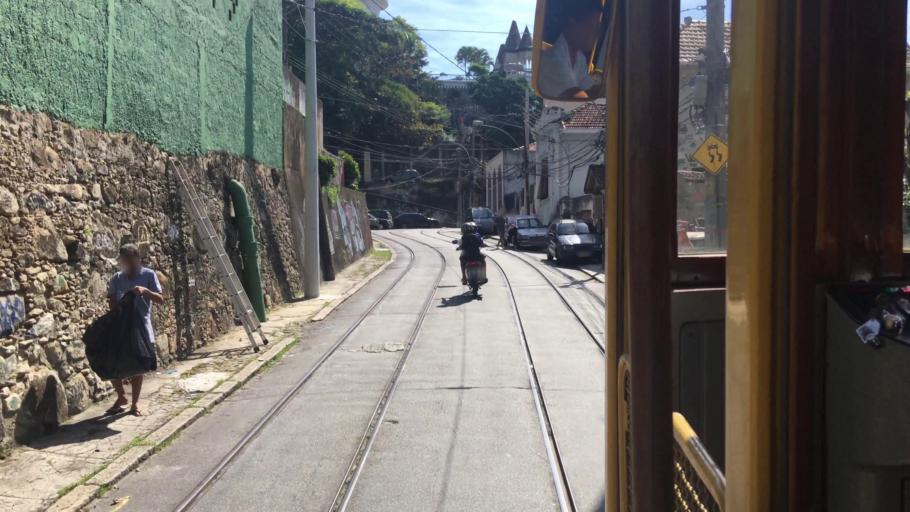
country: BR
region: Rio de Janeiro
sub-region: Rio De Janeiro
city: Rio de Janeiro
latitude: -22.9248
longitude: -43.1886
